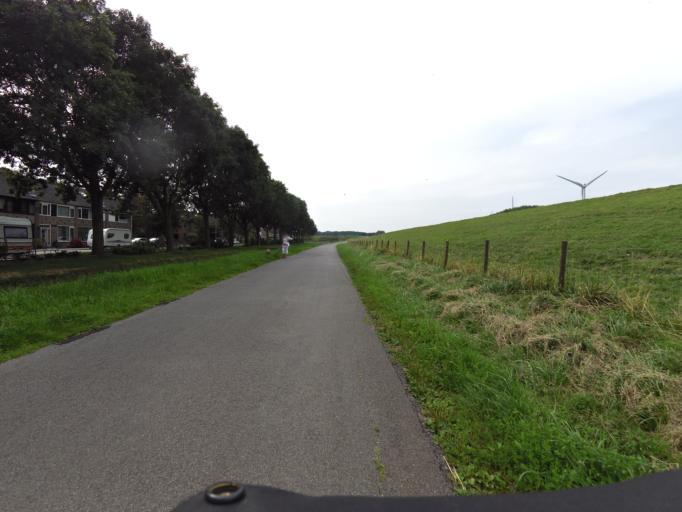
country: NL
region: South Holland
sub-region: Gemeente Maassluis
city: Maassluis
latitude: 51.8635
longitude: 4.2633
